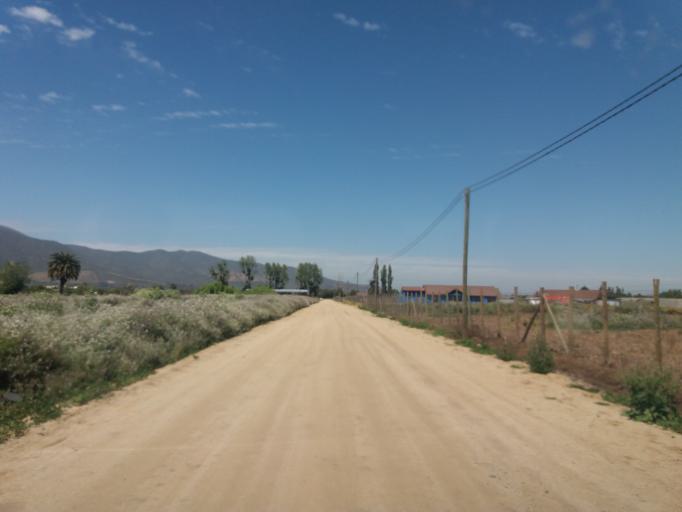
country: CL
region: Valparaiso
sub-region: Provincia de Quillota
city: Quillota
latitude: -32.8748
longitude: -71.2150
